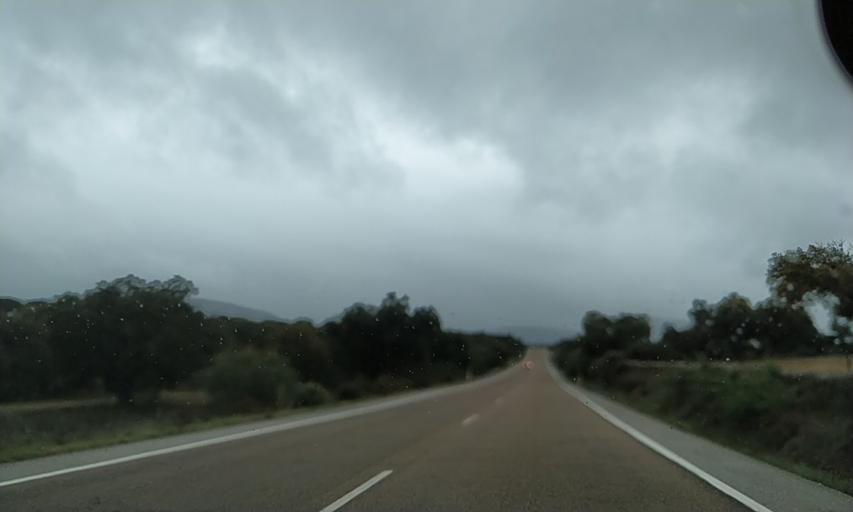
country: ES
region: Extremadura
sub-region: Provincia de Badajoz
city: Puebla de Obando
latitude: 39.2239
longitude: -6.5746
